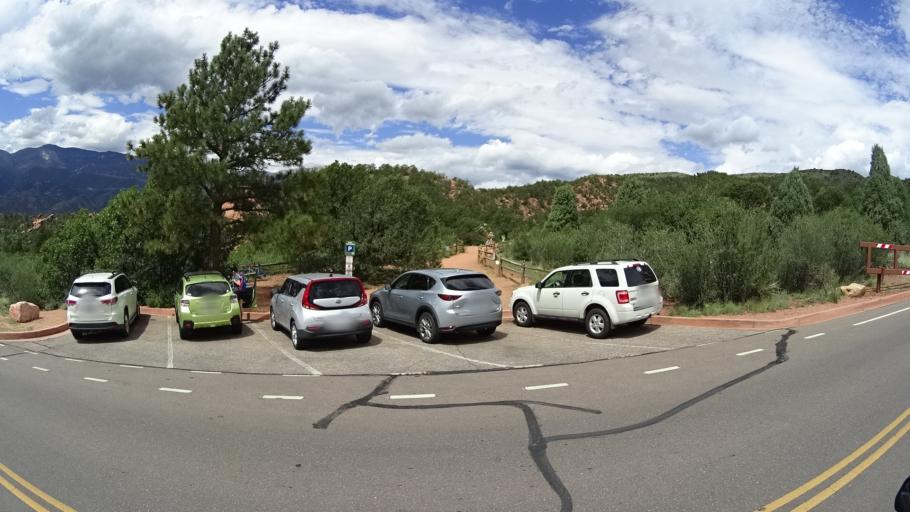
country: US
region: Colorado
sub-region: El Paso County
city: Manitou Springs
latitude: 38.8763
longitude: -104.8836
